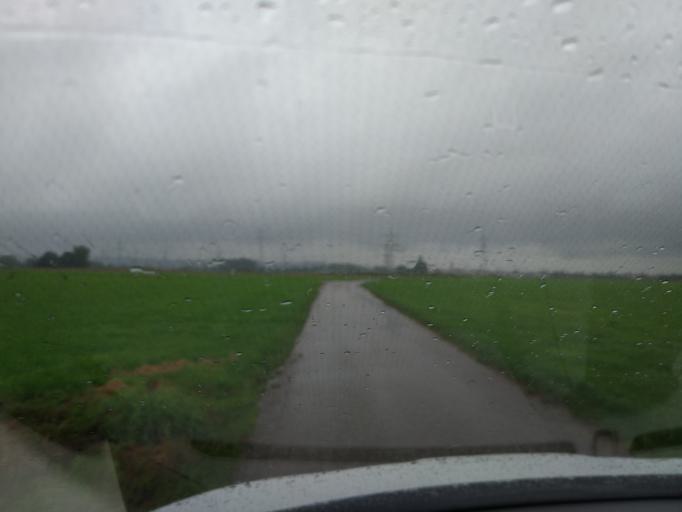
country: DE
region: Baden-Wuerttemberg
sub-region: Tuebingen Region
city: Achstetten
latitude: 48.2881
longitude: 9.9016
